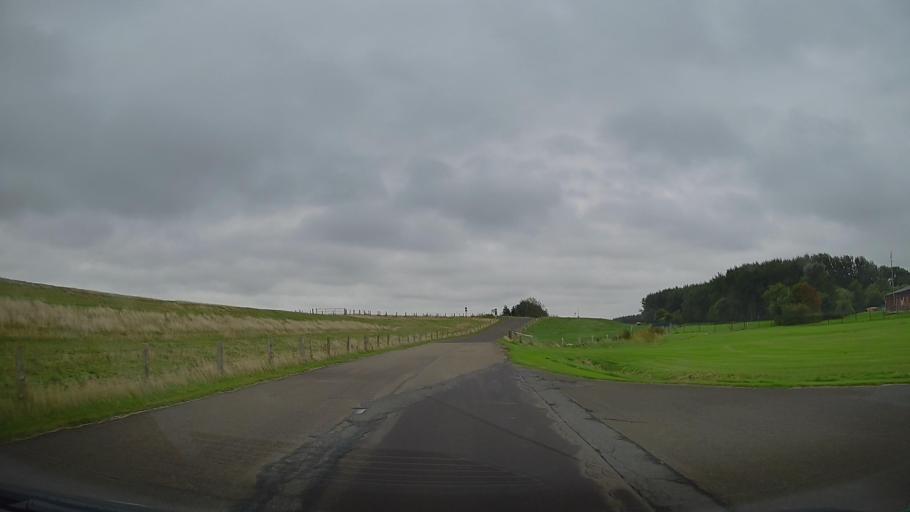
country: DE
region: Schleswig-Holstein
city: Elpersbuttel
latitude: 54.0709
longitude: 9.0126
